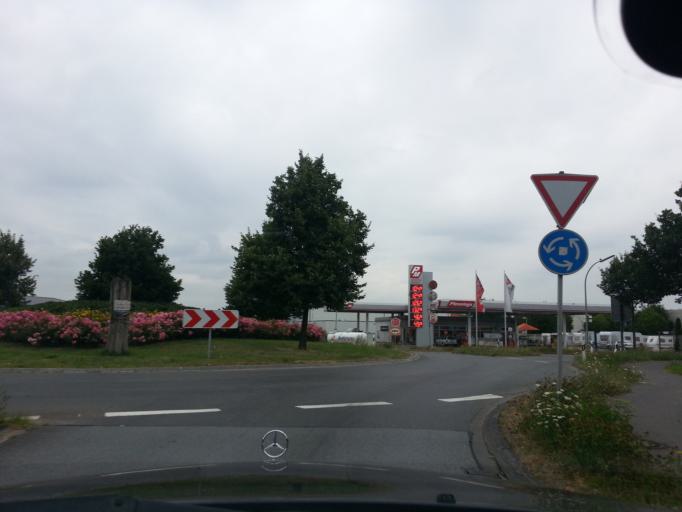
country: DE
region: North Rhine-Westphalia
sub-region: Regierungsbezirk Munster
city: Raesfeld
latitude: 51.7662
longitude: 6.8504
